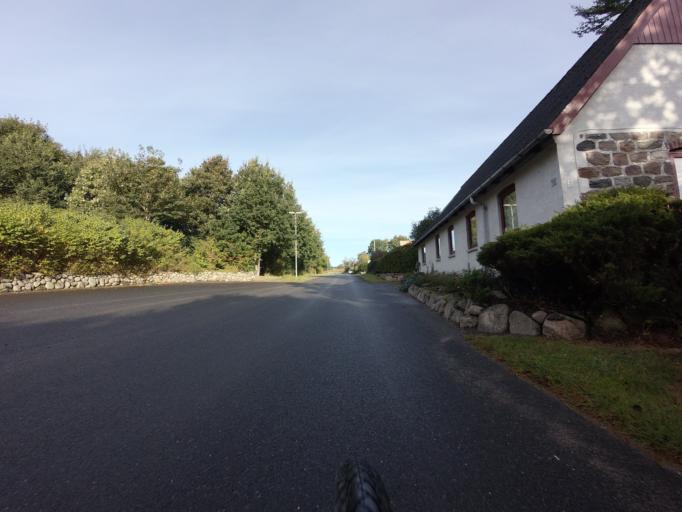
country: DK
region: Central Jutland
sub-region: Viborg Kommune
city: Bjerringbro
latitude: 56.4433
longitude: 9.5573
